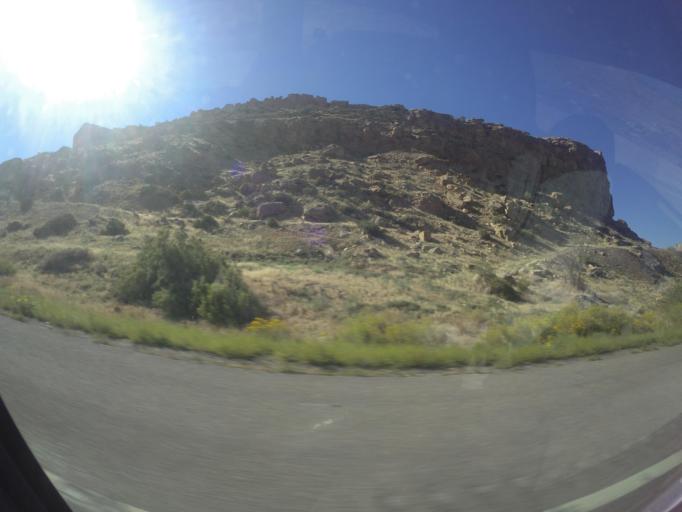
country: US
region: Colorado
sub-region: Mesa County
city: Palisade
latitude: 39.1212
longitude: -108.3225
